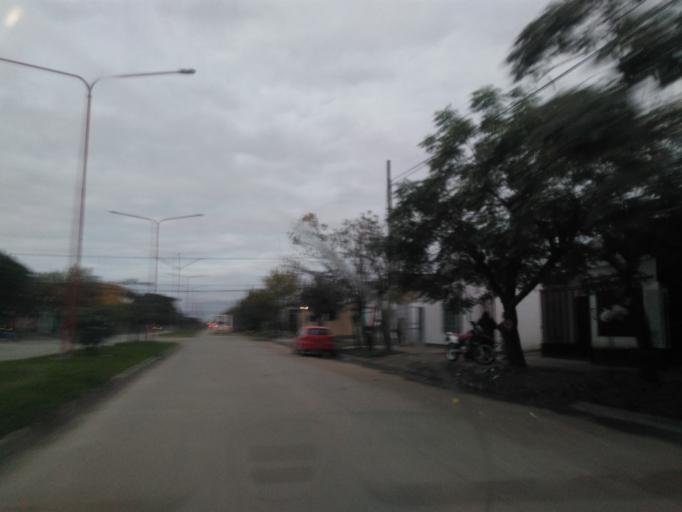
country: AR
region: Chaco
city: Resistencia
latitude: -27.4772
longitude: -58.9959
